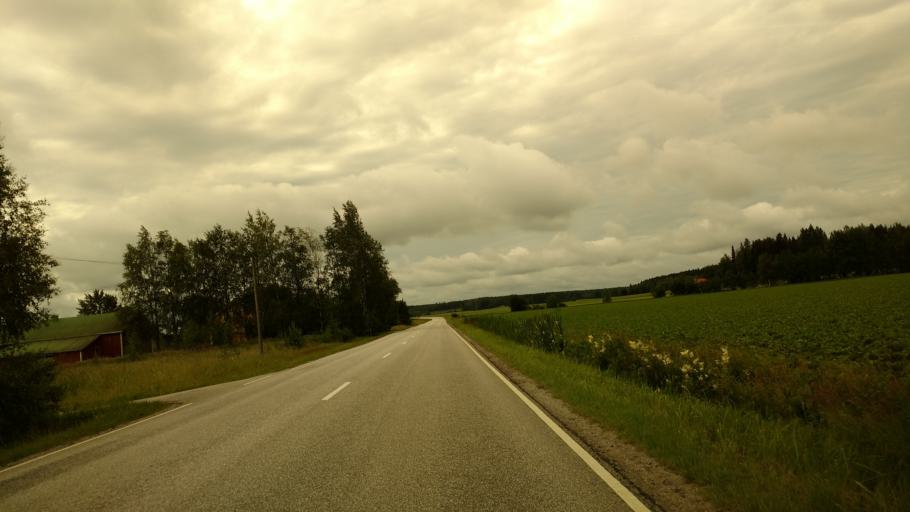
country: FI
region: Varsinais-Suomi
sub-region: Salo
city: Kuusjoki
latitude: 60.4774
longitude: 23.1594
